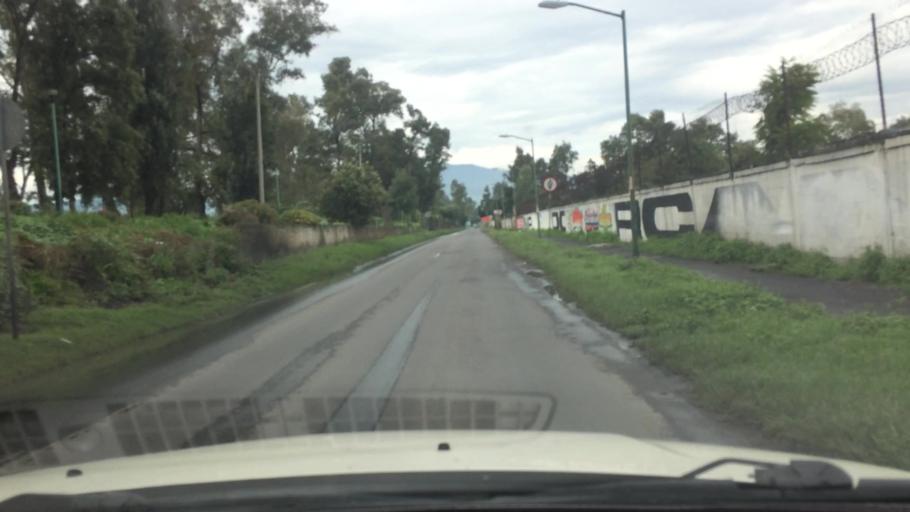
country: MX
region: Mexico City
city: Xochimilco
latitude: 19.3052
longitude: -99.1004
